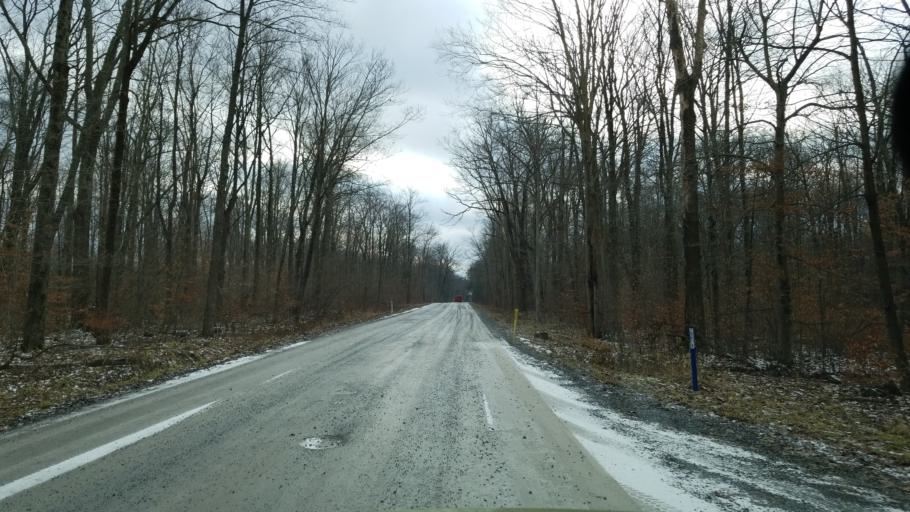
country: US
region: Pennsylvania
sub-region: Clearfield County
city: Clearfield
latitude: 41.1380
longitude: -78.5194
